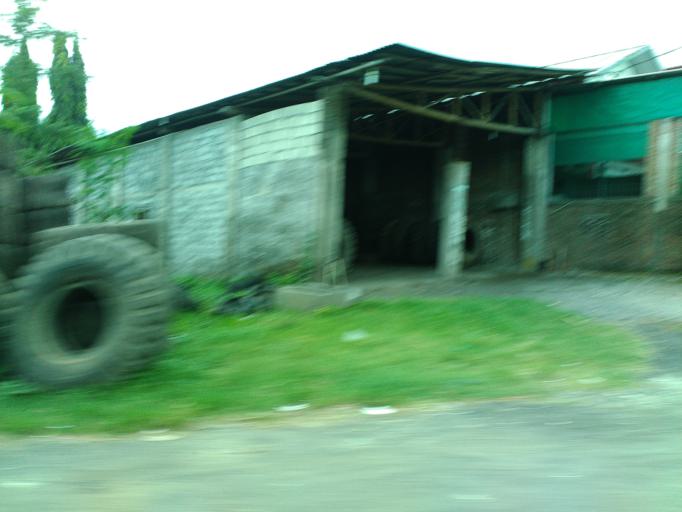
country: ID
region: Central Java
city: Gatak
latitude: -7.5865
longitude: 110.7112
